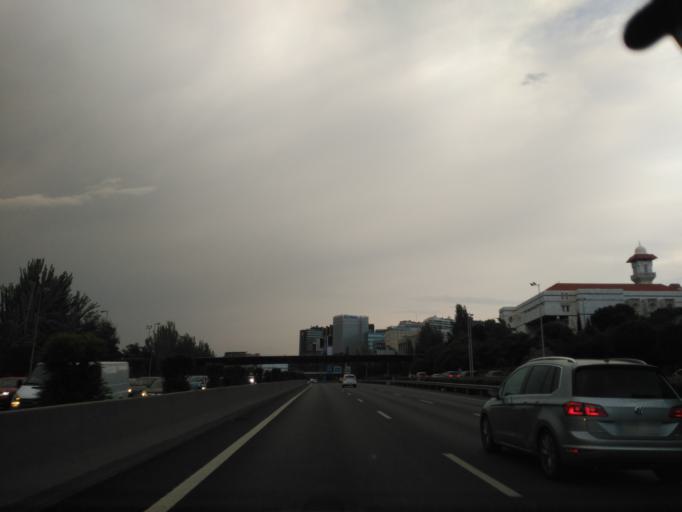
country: ES
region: Madrid
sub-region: Provincia de Madrid
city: Ciudad Lineal
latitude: 40.4370
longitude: -3.6595
